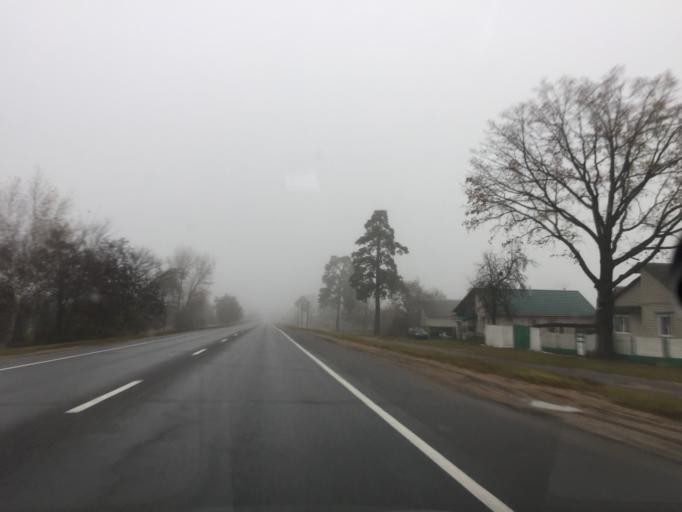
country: BY
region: Mogilev
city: Palykavichy Pyershyya
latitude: 54.0320
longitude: 30.4634
